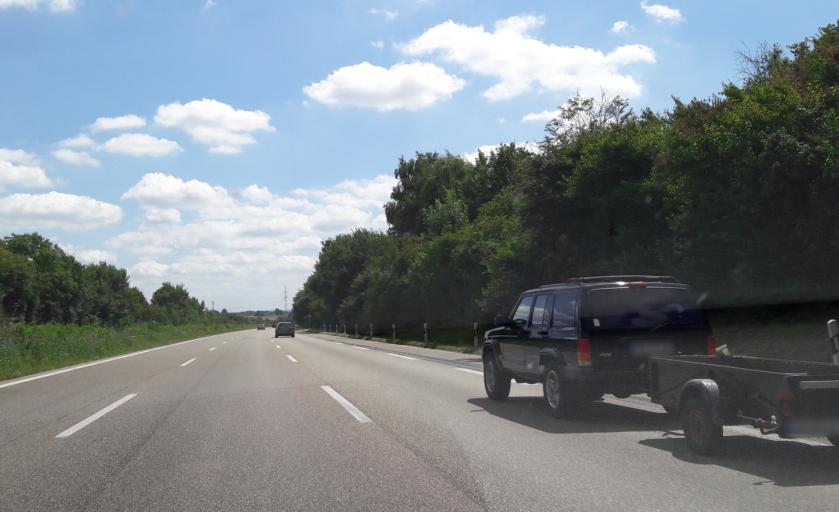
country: DE
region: Baden-Wuerttemberg
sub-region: Regierungsbezirk Stuttgart
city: Bad Rappenau
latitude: 49.1930
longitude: 9.1088
